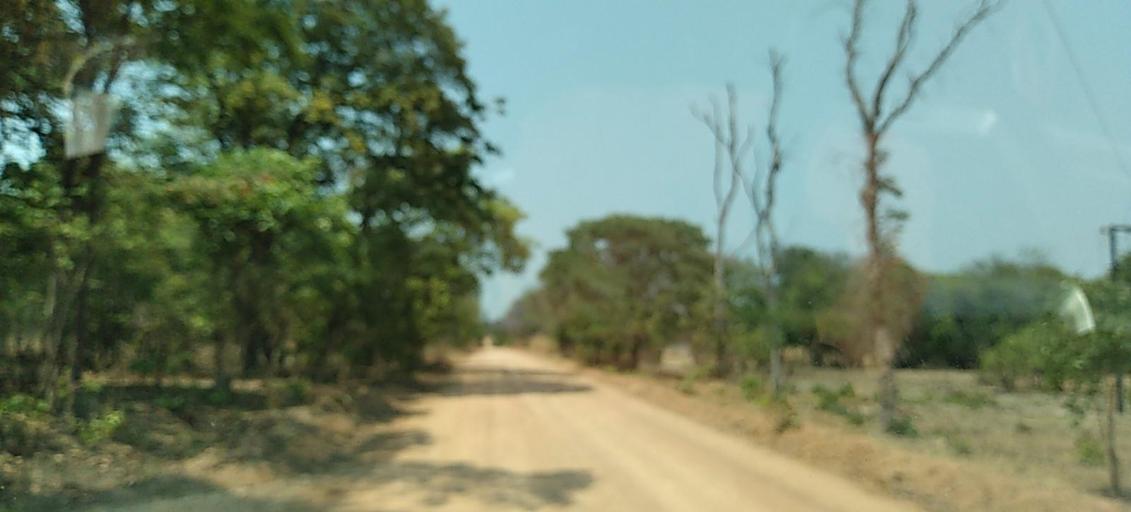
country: ZM
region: Copperbelt
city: Chambishi
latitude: -12.6149
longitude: 27.9570
